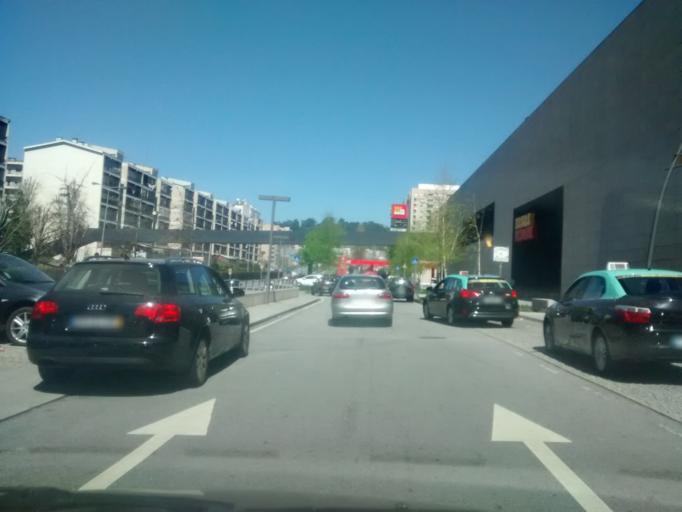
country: PT
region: Braga
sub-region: Braga
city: Braga
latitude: 41.5568
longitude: -8.4069
